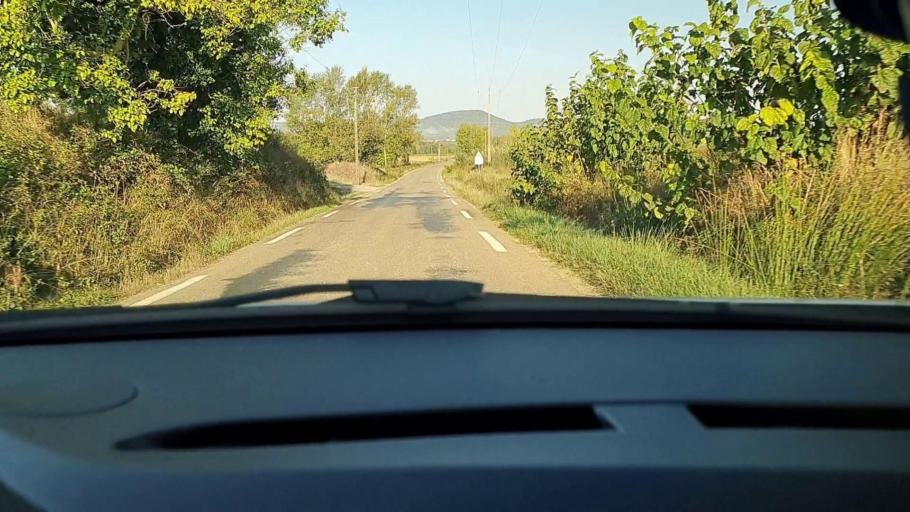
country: FR
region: Languedoc-Roussillon
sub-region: Departement du Gard
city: Barjac
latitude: 44.2613
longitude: 4.2847
